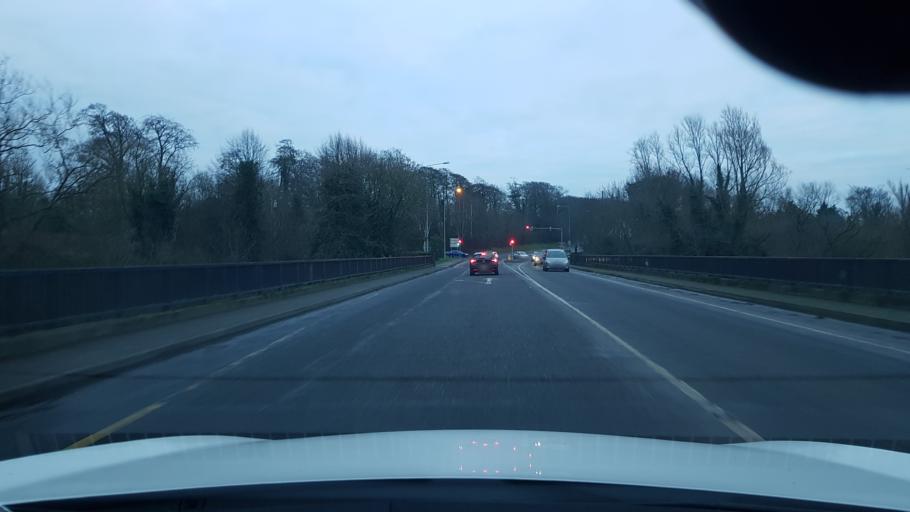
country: IE
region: Leinster
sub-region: An Mhi
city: Navan
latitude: 53.6313
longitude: -6.6620
